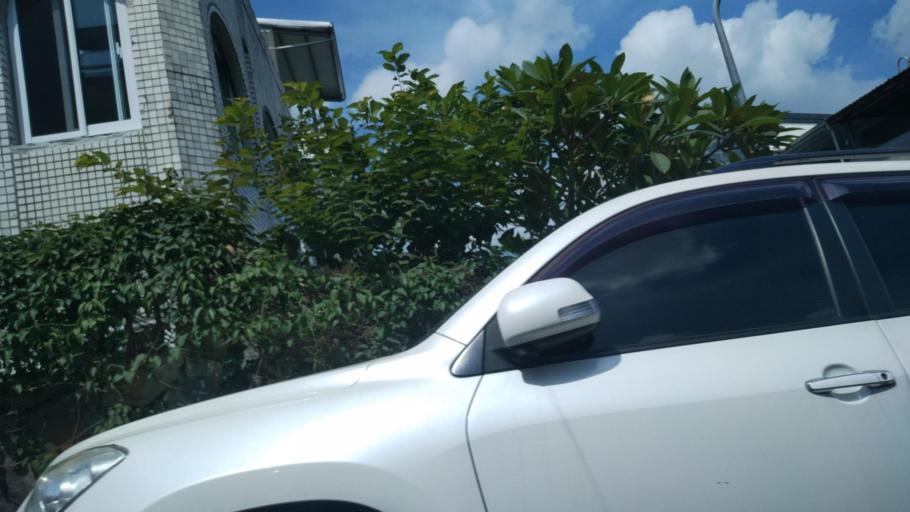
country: TW
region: Taipei
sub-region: Taipei
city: Banqiao
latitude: 24.9469
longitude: 121.5002
